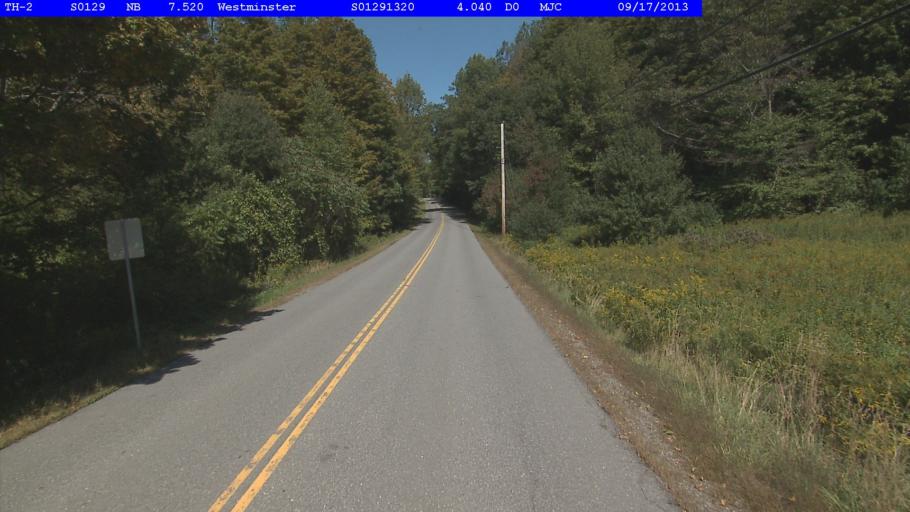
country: US
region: Vermont
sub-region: Windham County
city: Bellows Falls
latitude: 43.0736
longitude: -72.5393
